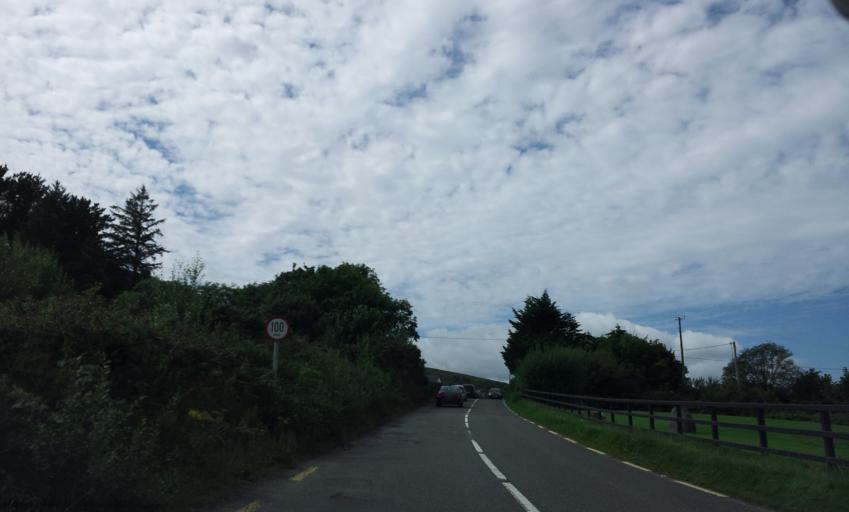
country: IE
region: Munster
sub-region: Ciarrai
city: Killorglin
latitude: 52.0642
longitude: -9.9125
